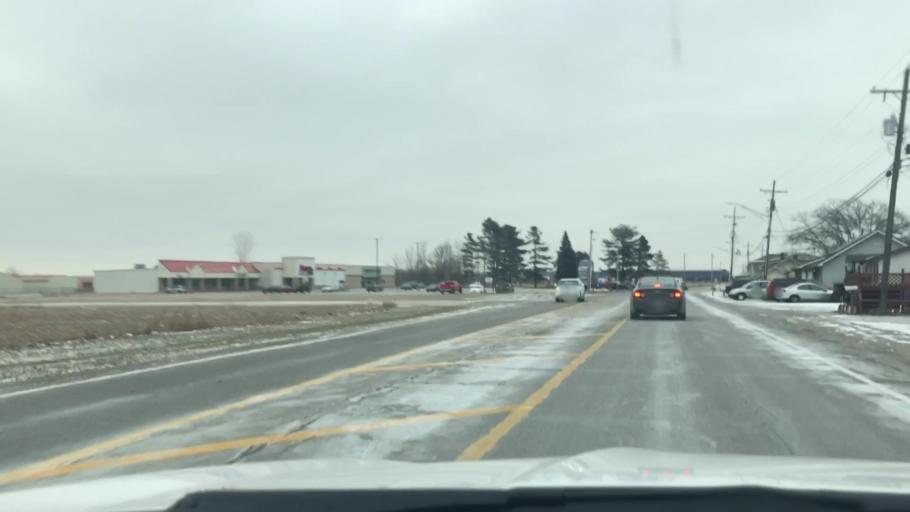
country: US
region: Indiana
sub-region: Fulton County
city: Rochester
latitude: 41.0620
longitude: -86.1844
